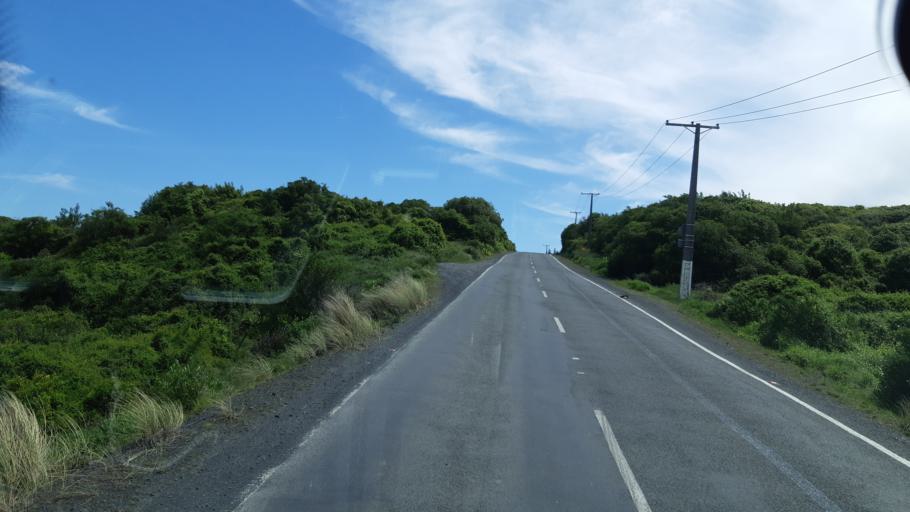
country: NZ
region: Otago
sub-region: Dunedin City
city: Dunedin
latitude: -45.9271
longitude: 170.4264
